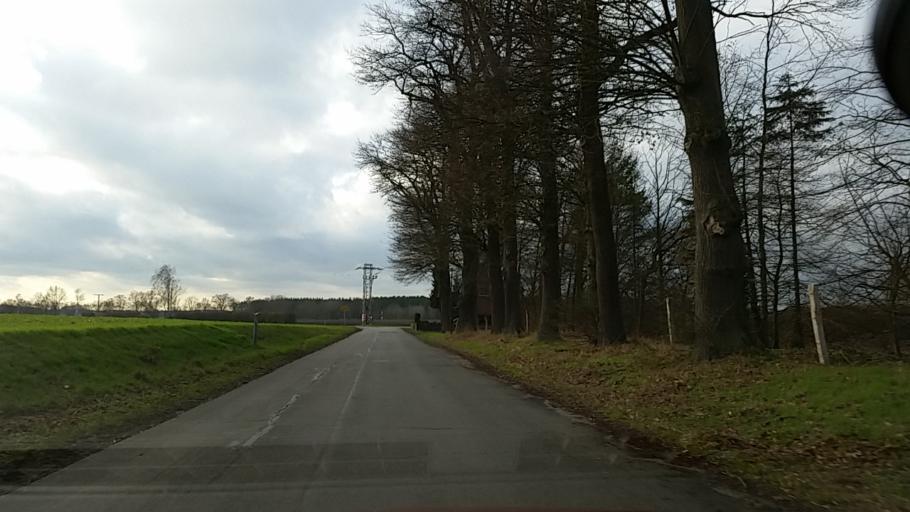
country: DE
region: Lower Saxony
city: Luder
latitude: 52.7652
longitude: 10.6874
